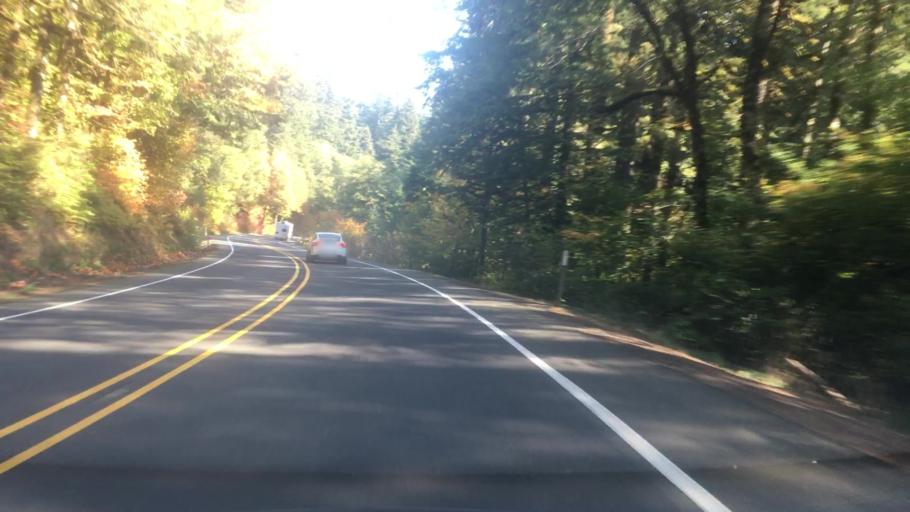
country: US
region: Oregon
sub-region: Lincoln County
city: Rose Lodge
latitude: 45.0551
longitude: -123.7573
